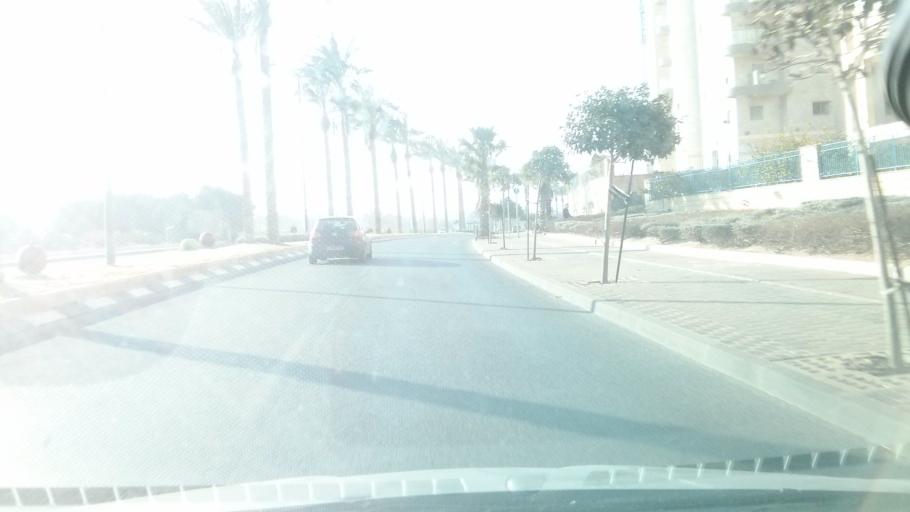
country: IL
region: Central District
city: Netanya
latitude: 32.3158
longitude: 34.8480
